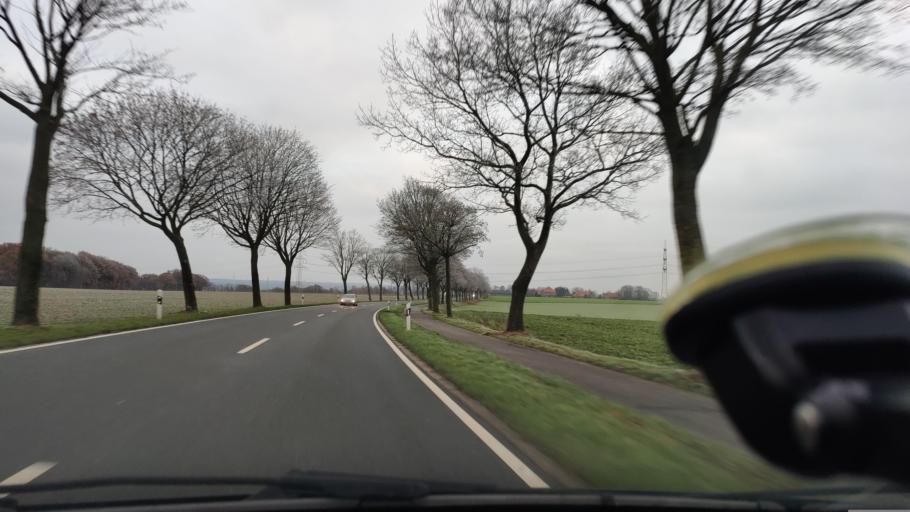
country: DE
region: North Rhine-Westphalia
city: Kalkar
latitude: 51.7184
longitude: 6.3022
